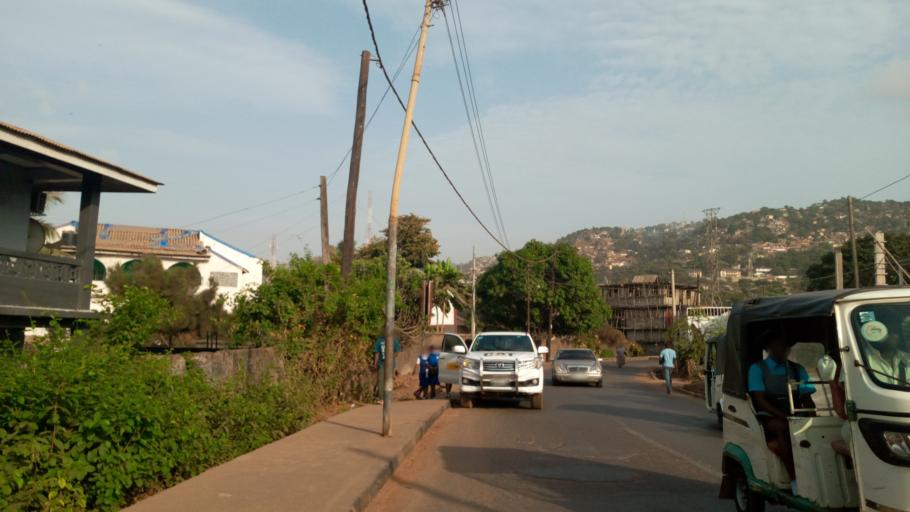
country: SL
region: Western Area
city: Freetown
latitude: 8.4739
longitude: -13.2523
